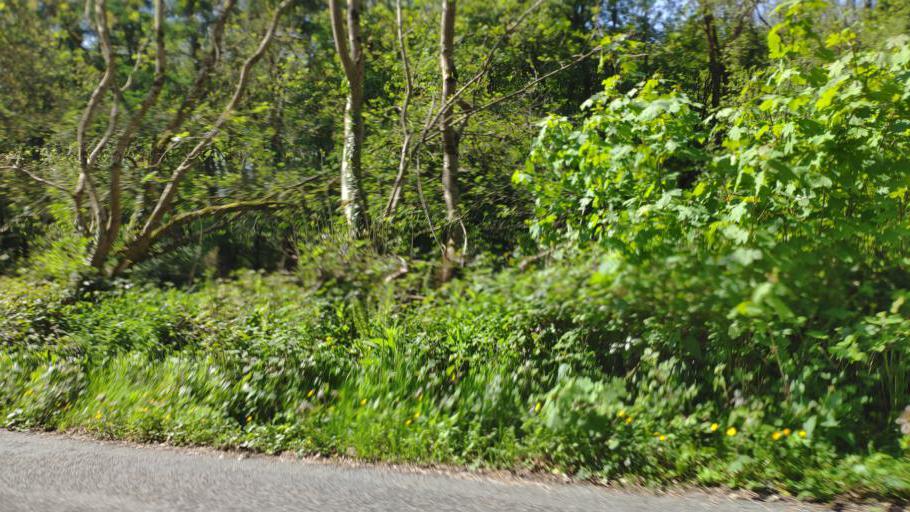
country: IE
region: Munster
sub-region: County Cork
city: Blarney
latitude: 51.9804
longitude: -8.5862
